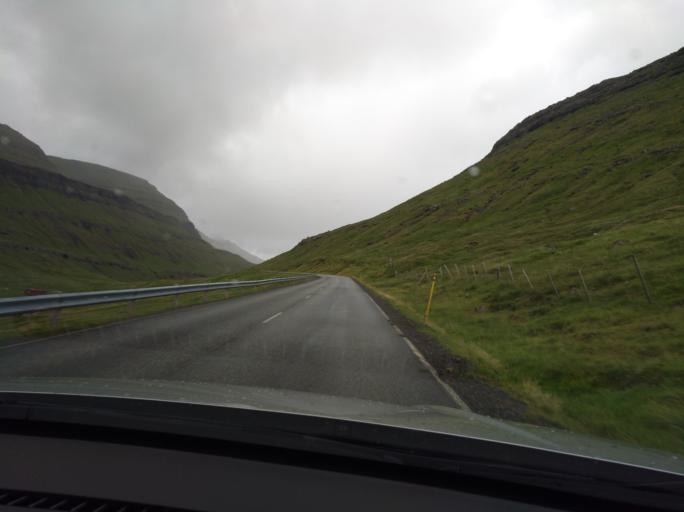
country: FO
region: Eysturoy
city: Fuglafjordur
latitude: 62.2280
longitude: -6.8790
